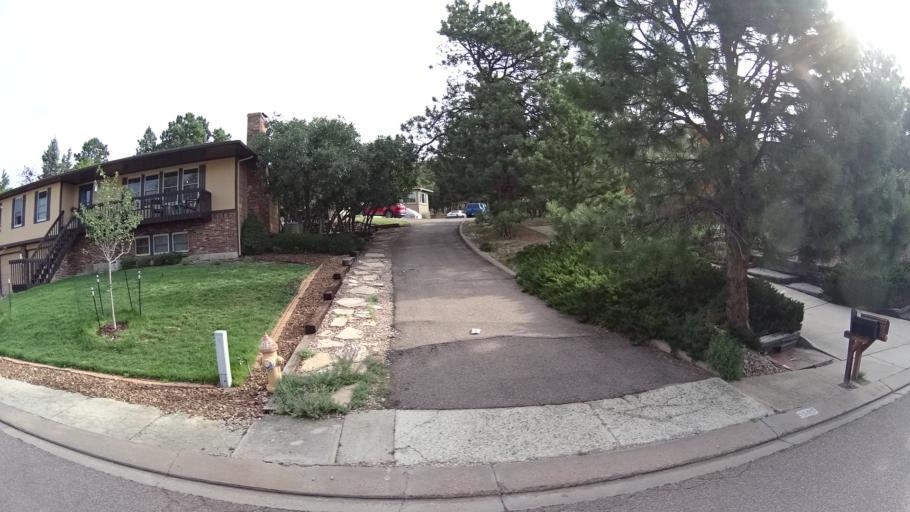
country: US
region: Colorado
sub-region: El Paso County
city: Air Force Academy
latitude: 38.9324
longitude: -104.8432
